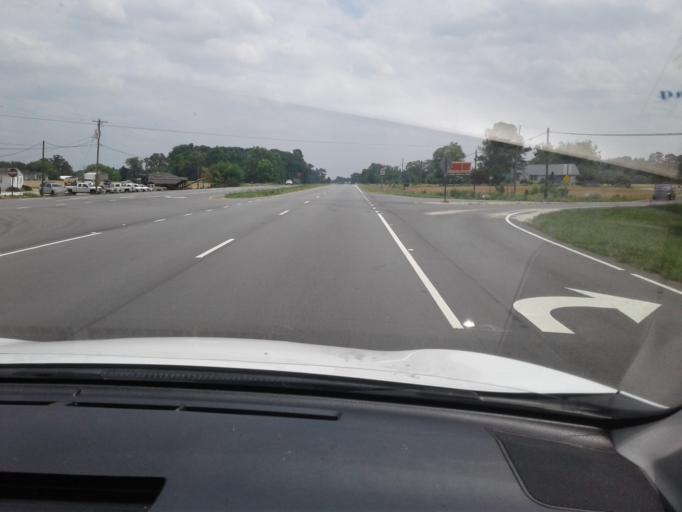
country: US
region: North Carolina
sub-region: Harnett County
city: Erwin
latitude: 35.3671
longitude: -78.7050
